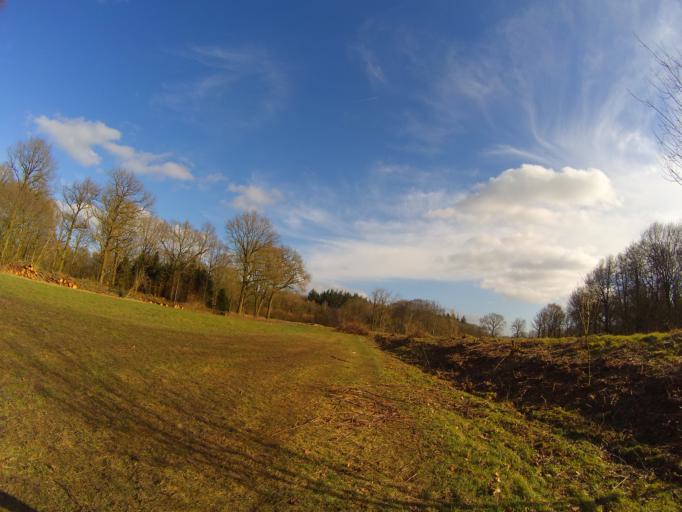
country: NL
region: Gelderland
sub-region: Gemeente Barneveld
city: Terschuur
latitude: 52.1469
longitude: 5.5365
